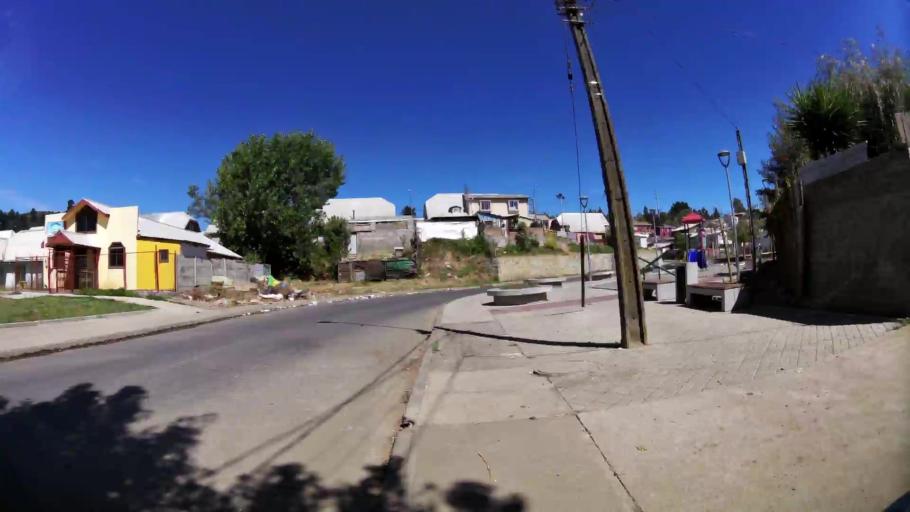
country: CL
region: Biobio
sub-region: Provincia de Concepcion
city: Penco
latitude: -36.7281
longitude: -72.9824
